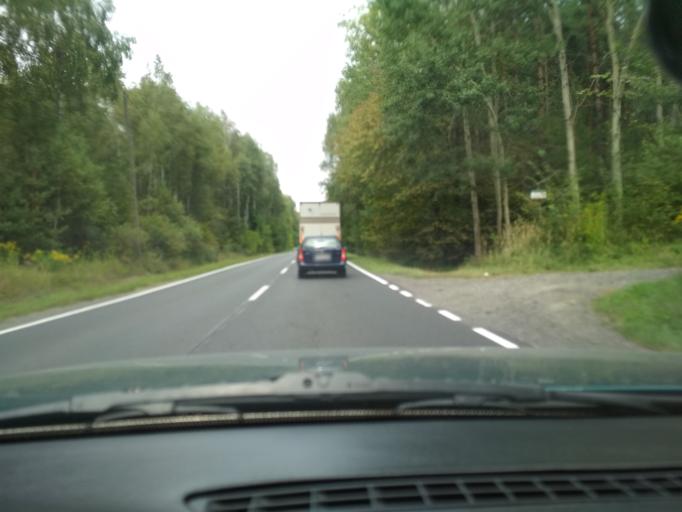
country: PL
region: Silesian Voivodeship
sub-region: Powiat zawiercianski
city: Zawiercie
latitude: 50.4661
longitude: 19.3982
